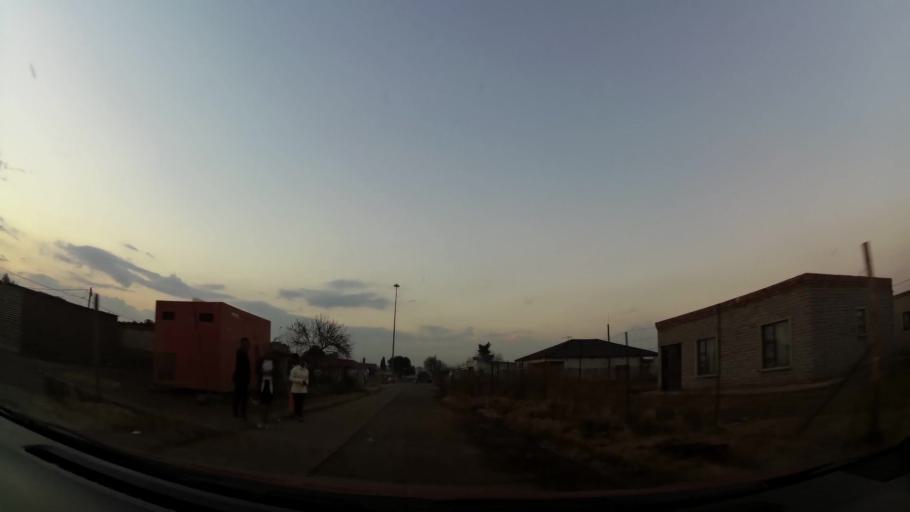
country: ZA
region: Gauteng
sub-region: City of Johannesburg Metropolitan Municipality
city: Orange Farm
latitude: -26.5497
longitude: 27.8488
